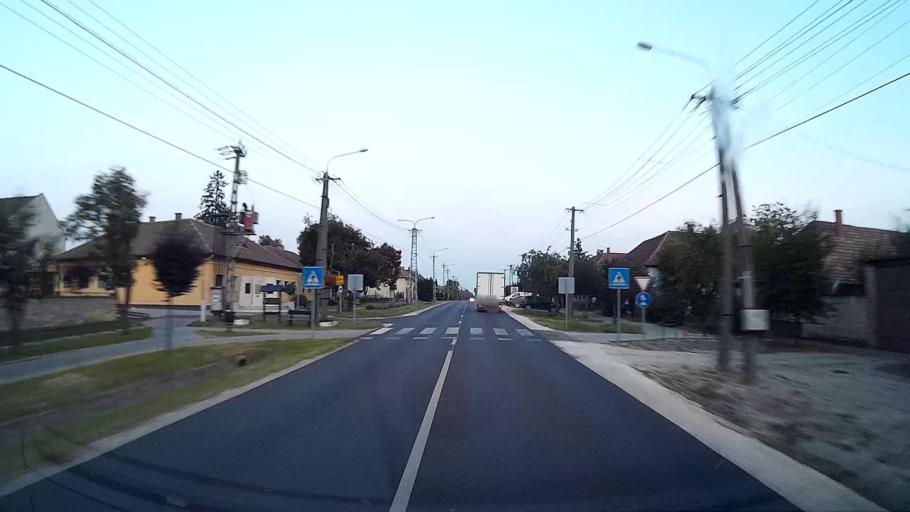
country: HU
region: Pest
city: Cegledbercel
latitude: 47.2160
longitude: 19.6750
